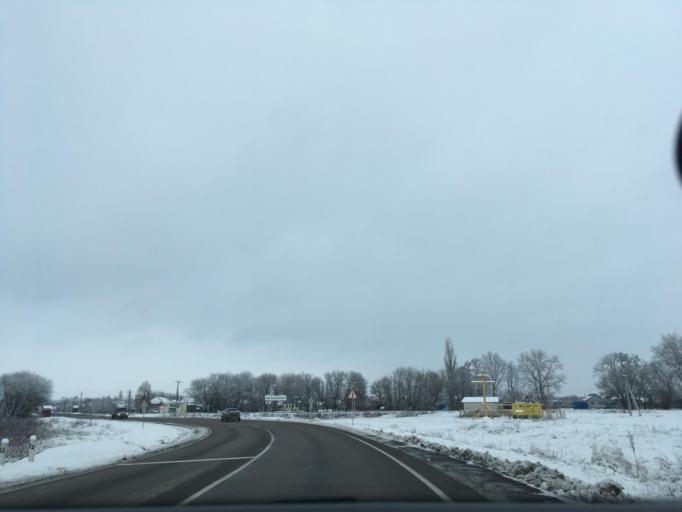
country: RU
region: Voronezj
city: Zabolotovka
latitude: 50.2468
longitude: 39.3525
